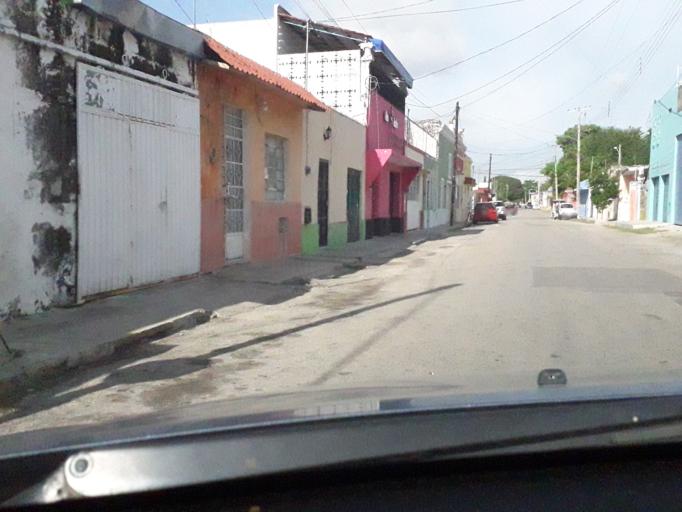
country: MX
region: Yucatan
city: Merida
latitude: 20.9553
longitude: -89.6144
